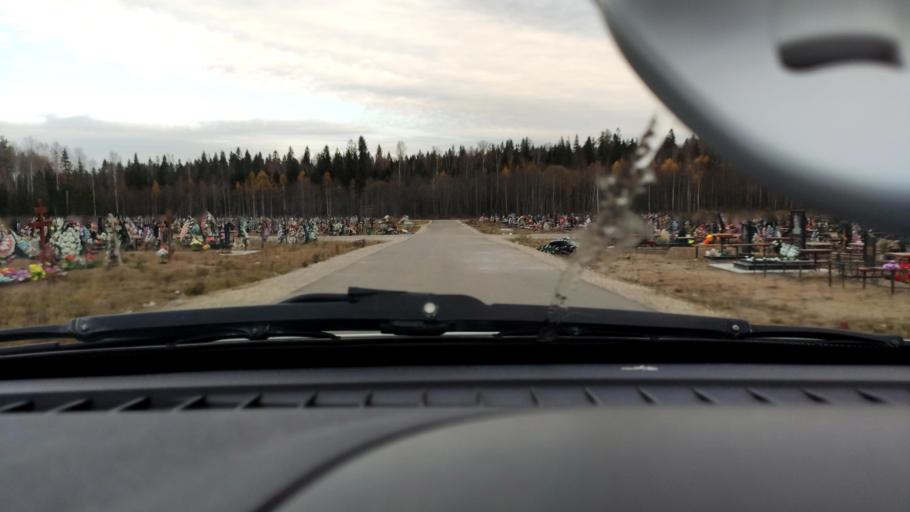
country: RU
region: Perm
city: Kondratovo
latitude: 58.0699
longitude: 56.1361
